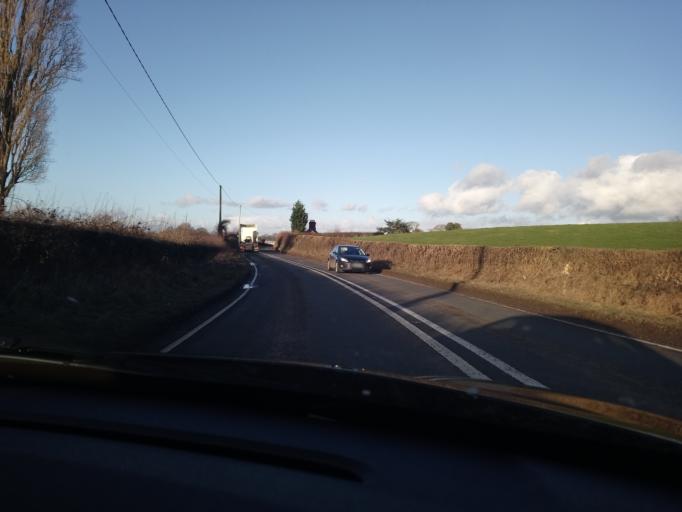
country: GB
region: England
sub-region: Shropshire
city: Ellesmere
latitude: 52.9067
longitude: -2.8487
